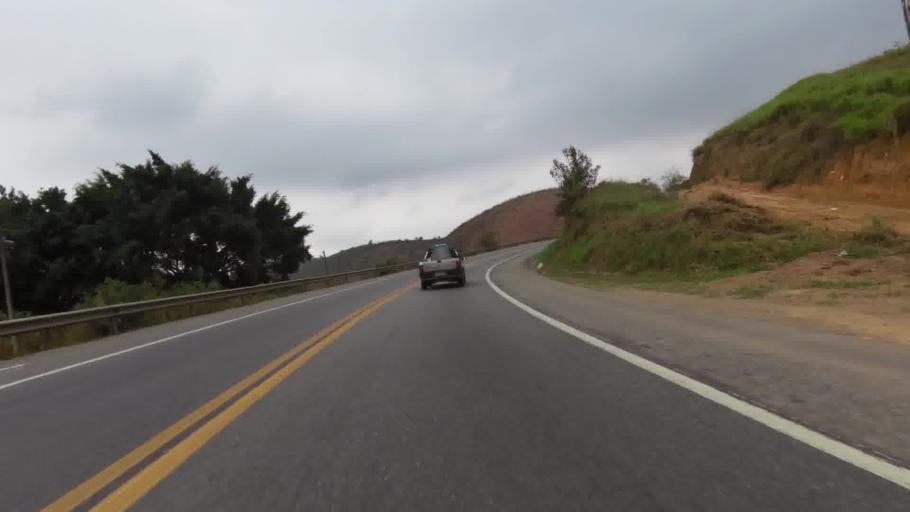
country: BR
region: Espirito Santo
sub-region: Rio Novo Do Sul
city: Rio Novo do Sul
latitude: -20.8891
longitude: -40.9854
